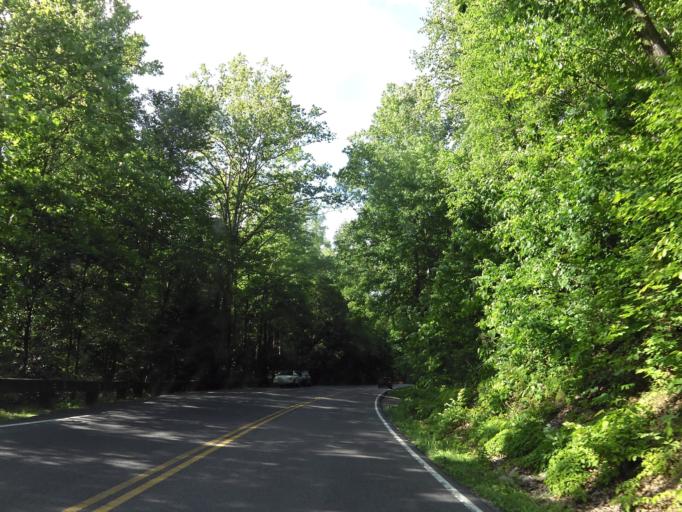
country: US
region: Tennessee
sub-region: Sevier County
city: Gatlinburg
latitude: 35.6994
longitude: -83.5268
